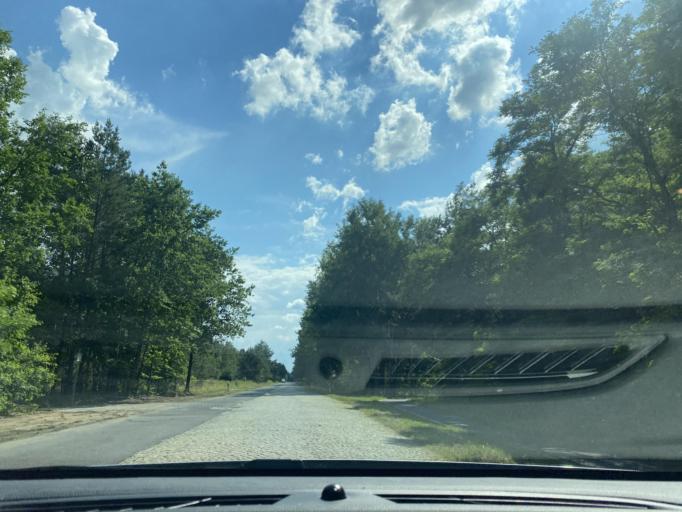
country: DE
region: Saxony
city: Boxberg
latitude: 51.4260
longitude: 14.5937
